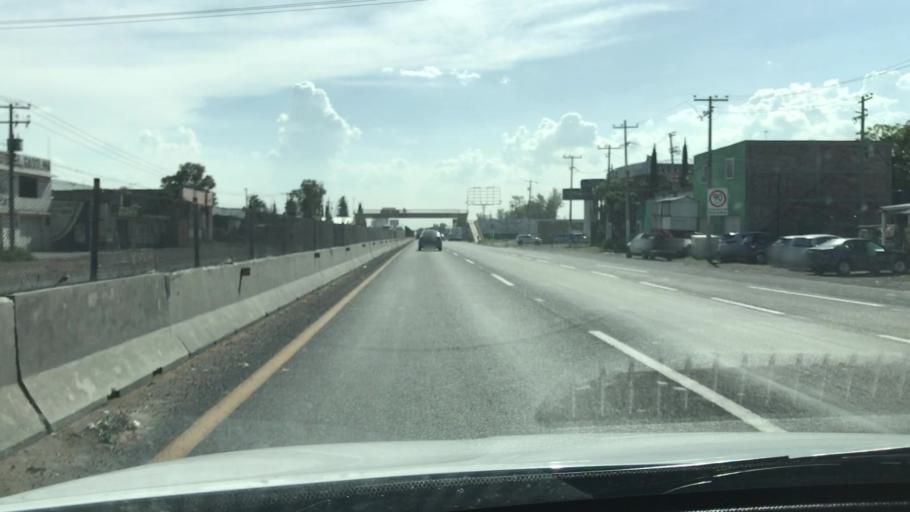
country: MX
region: Guanajuato
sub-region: Celaya
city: Colonia Pedro Maria Anaya
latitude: 20.5166
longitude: -100.8783
